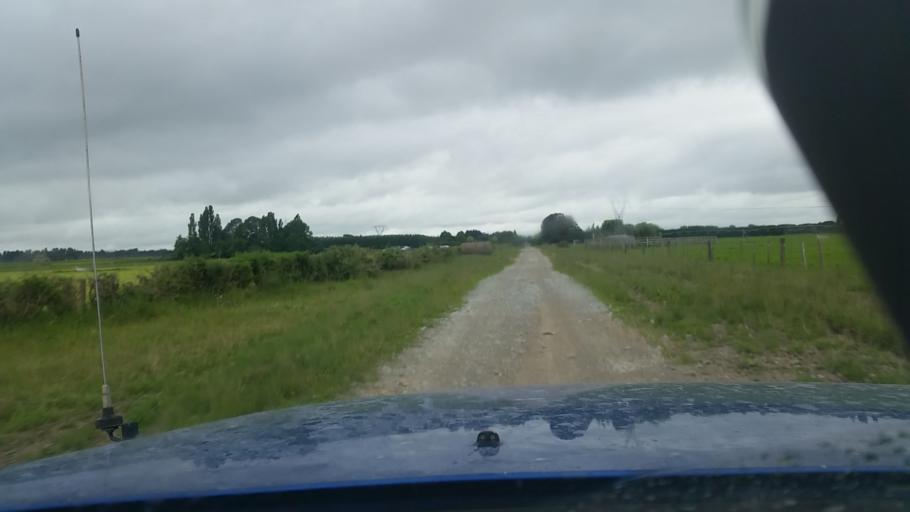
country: NZ
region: Canterbury
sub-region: Ashburton District
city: Ashburton
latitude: -43.8438
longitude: 171.6818
